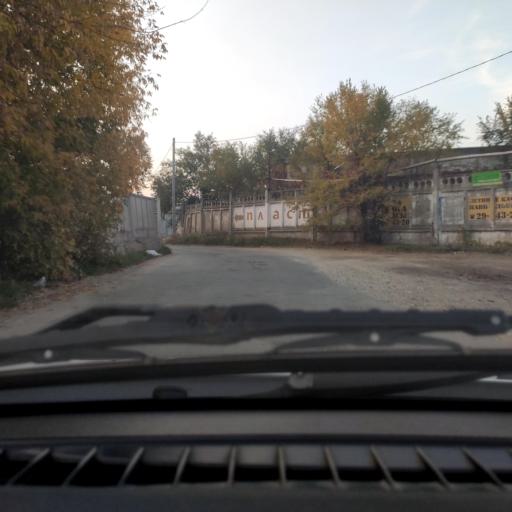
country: RU
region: Samara
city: Zhigulevsk
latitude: 53.4851
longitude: 49.4915
